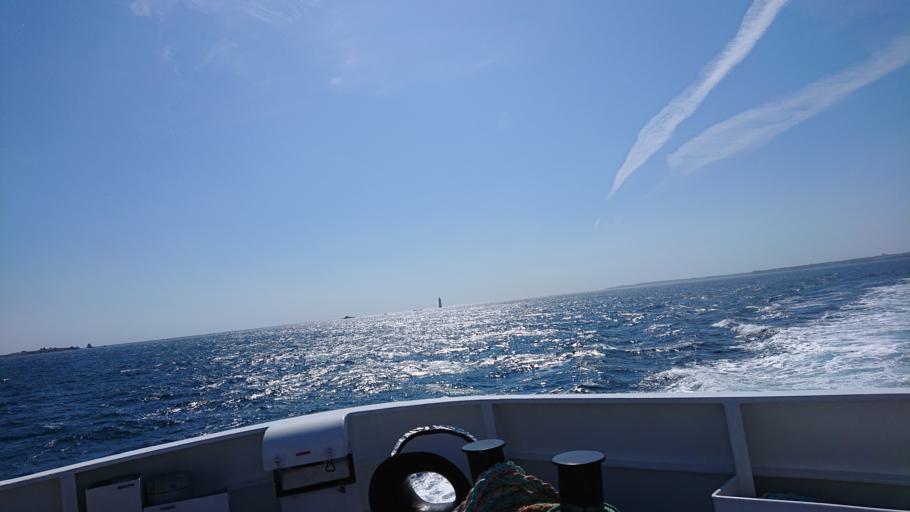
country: FR
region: Brittany
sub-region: Departement du Finistere
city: Lampaul-Plouarzel
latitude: 48.4457
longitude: -4.9958
